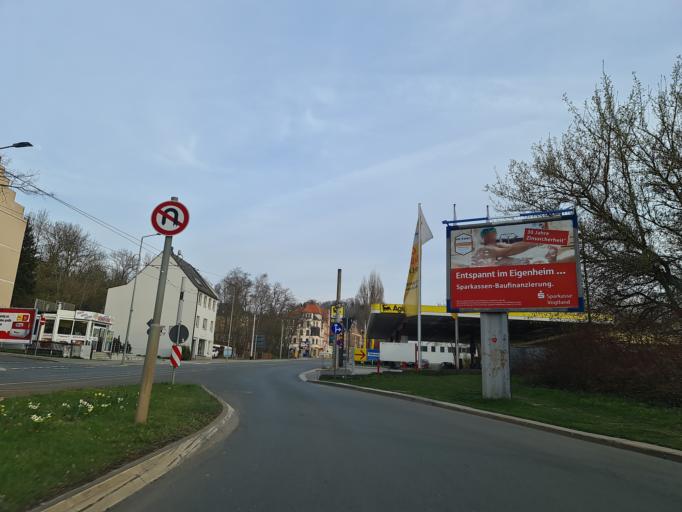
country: DE
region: Saxony
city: Plauen
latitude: 50.4856
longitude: 12.1388
